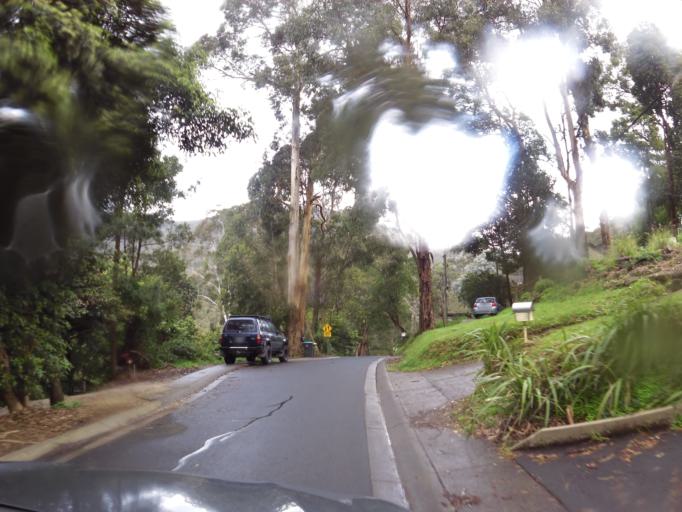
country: AU
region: Victoria
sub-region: Knox
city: The Basin
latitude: -37.8621
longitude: 145.3202
